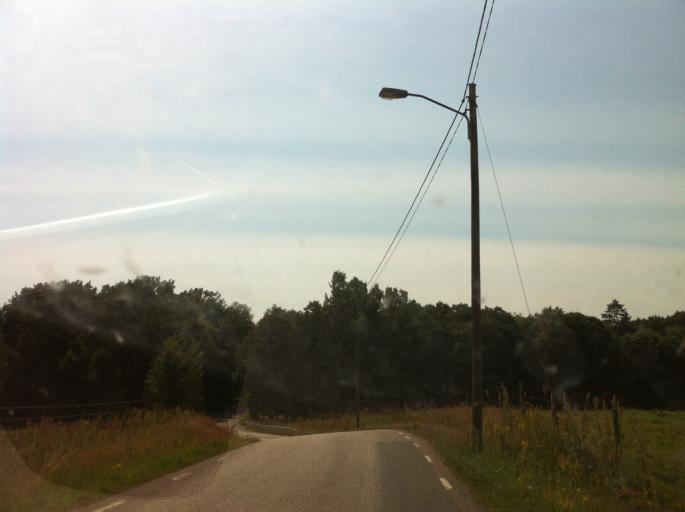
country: SE
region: Skane
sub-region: Hoors Kommun
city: Hoeoer
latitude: 56.0169
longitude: 13.5037
